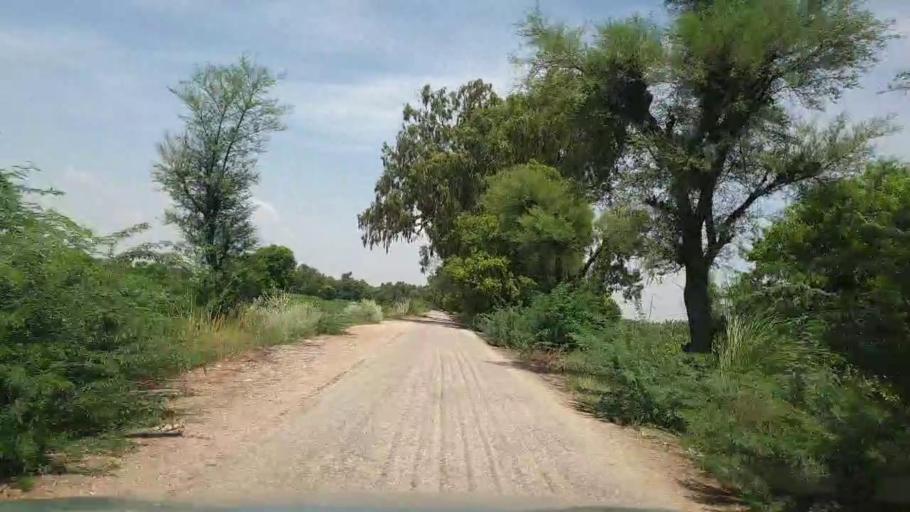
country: PK
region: Sindh
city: Bozdar
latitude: 27.0842
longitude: 68.9747
